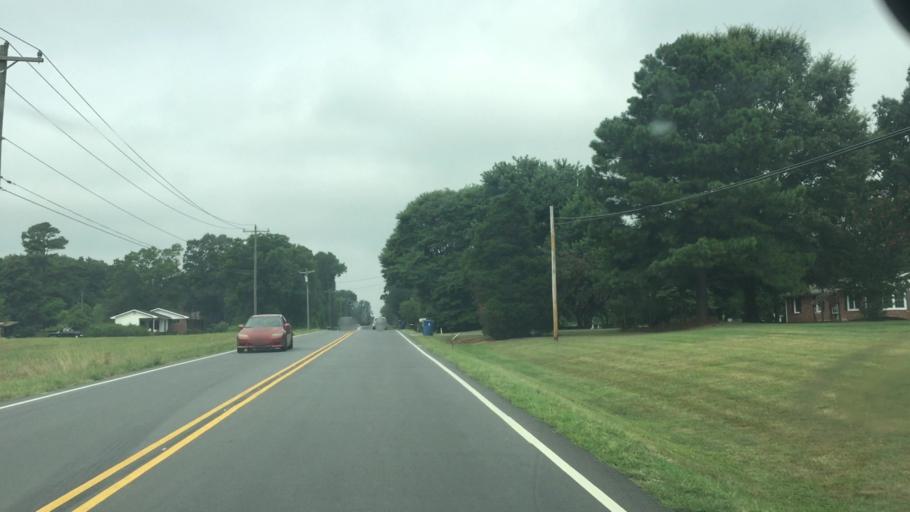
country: US
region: North Carolina
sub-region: Rowan County
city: Enochville
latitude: 35.4389
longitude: -80.7169
